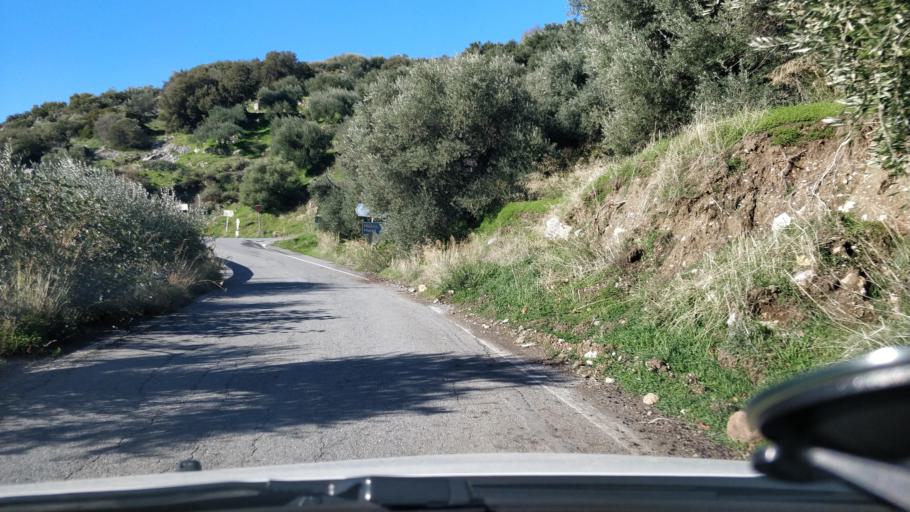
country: GR
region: Crete
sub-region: Nomos Lasithiou
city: Kritsa
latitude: 35.0794
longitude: 25.5813
